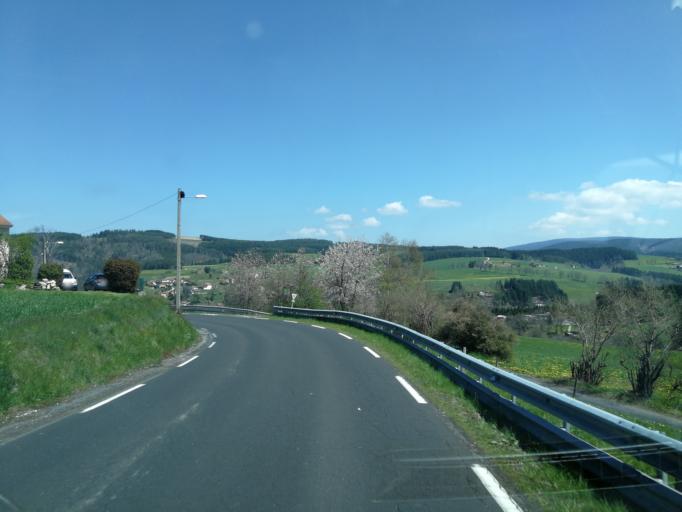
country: FR
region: Auvergne
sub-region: Departement de la Haute-Loire
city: Dunieres
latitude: 45.2082
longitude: 4.3467
